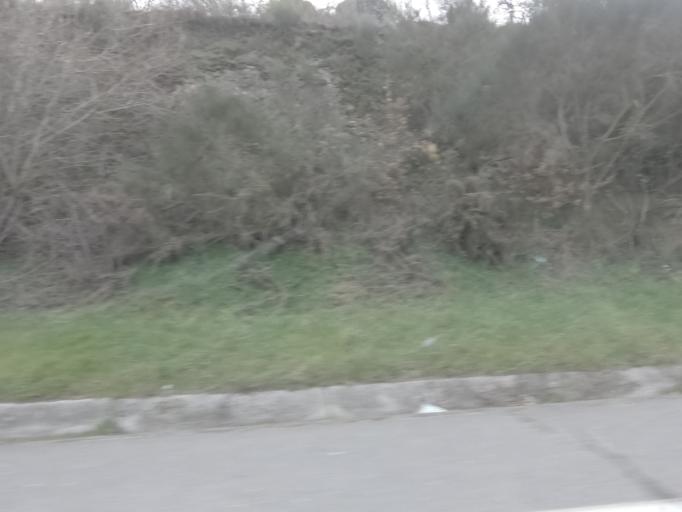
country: ES
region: Galicia
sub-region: Provincia de Ourense
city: Allariz
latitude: 42.1952
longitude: -7.7983
